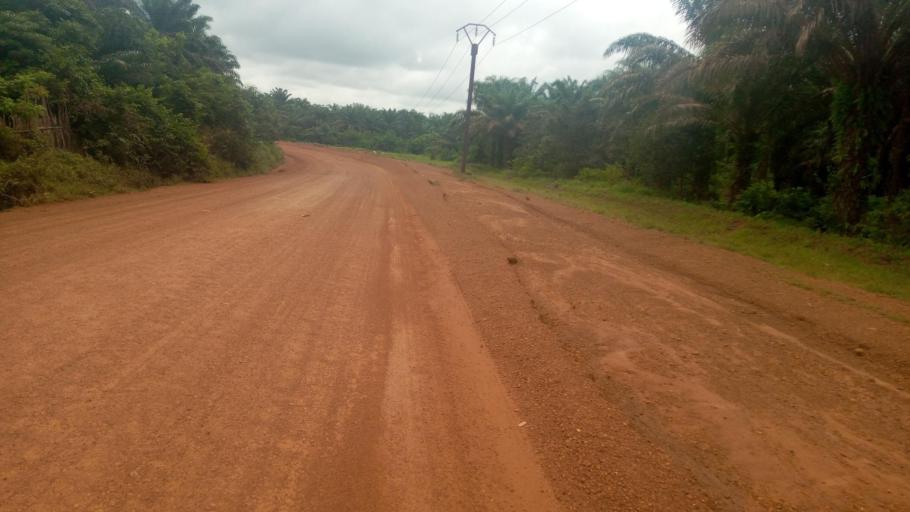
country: SL
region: Southern Province
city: Mogbwemo
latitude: 7.7255
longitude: -12.2789
